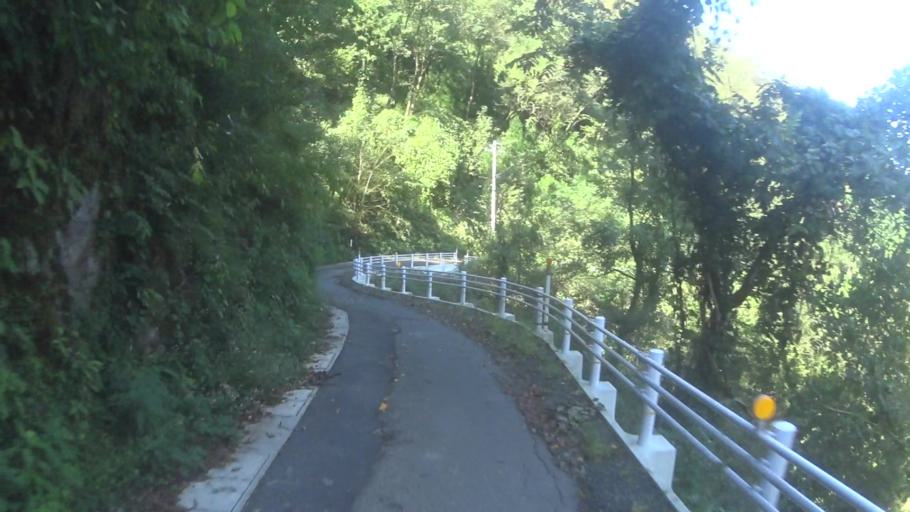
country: JP
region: Kyoto
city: Miyazu
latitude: 35.6534
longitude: 135.1587
